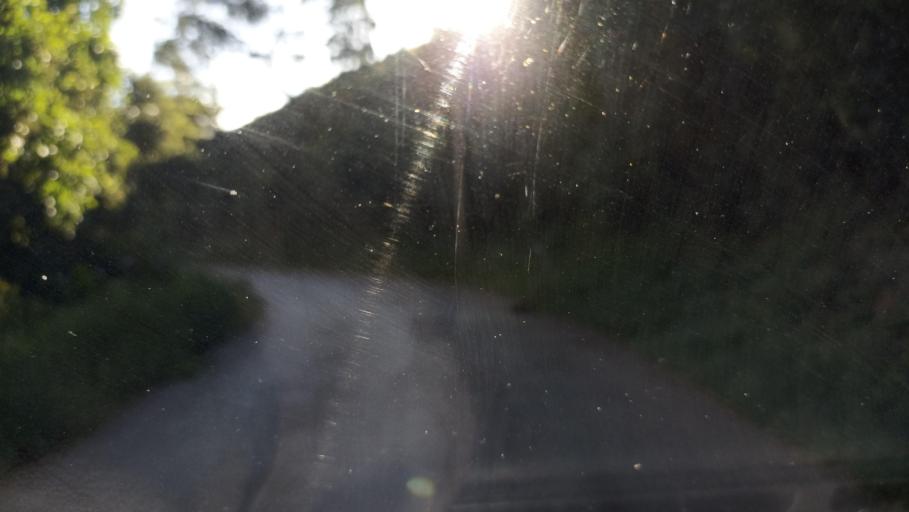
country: BR
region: Minas Gerais
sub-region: Ouro Preto
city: Ouro Preto
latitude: -20.3132
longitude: -43.5947
